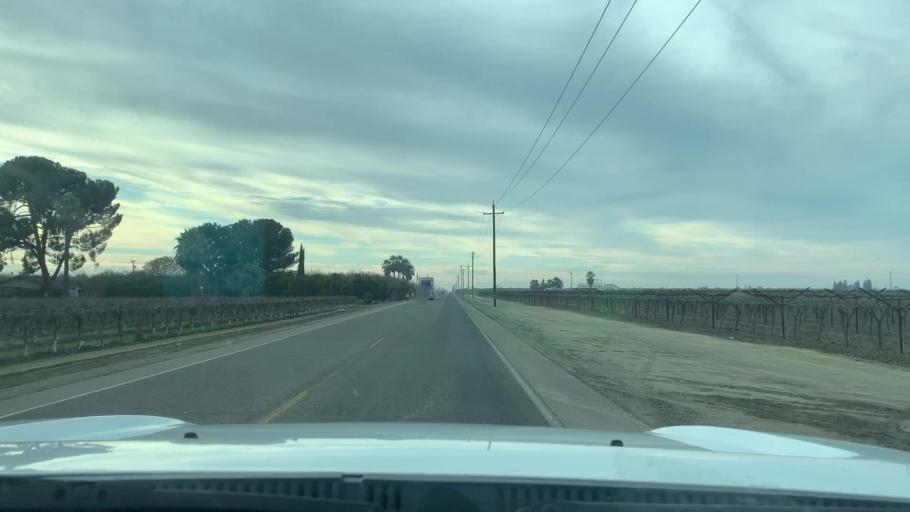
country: US
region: California
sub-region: Fresno County
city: Easton
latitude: 36.6054
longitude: -119.7595
